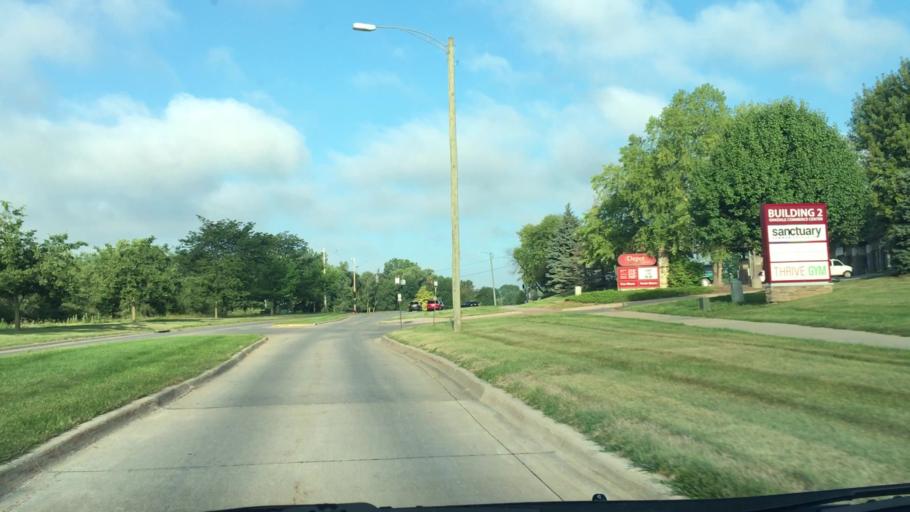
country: US
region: Iowa
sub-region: Johnson County
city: Coralville
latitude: 41.7017
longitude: -91.5609
